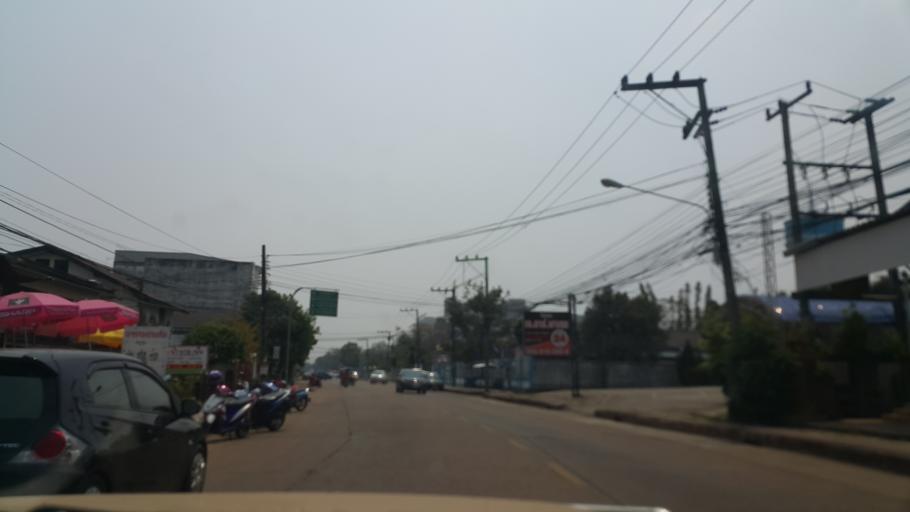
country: TH
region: Nakhon Phanom
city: Nakhon Phanom
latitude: 17.4164
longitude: 104.7771
